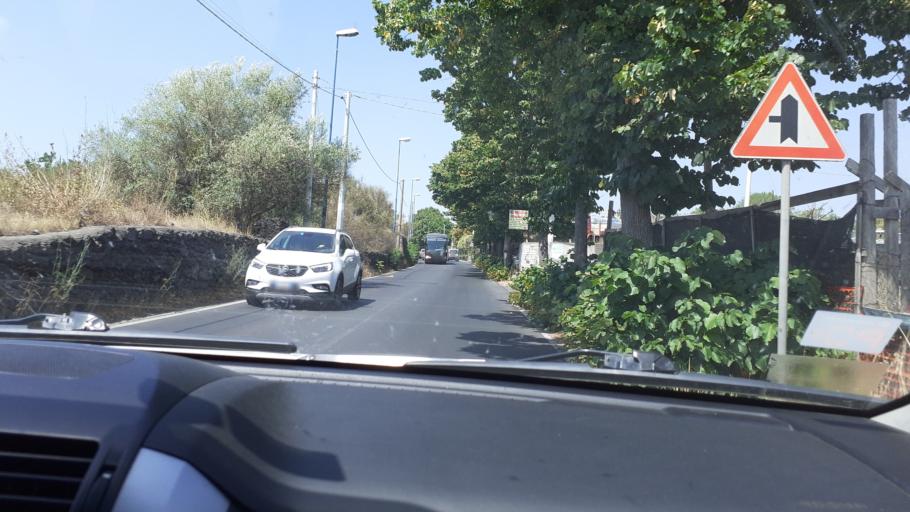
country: IT
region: Sicily
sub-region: Catania
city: Pedara
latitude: 37.6155
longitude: 15.0449
